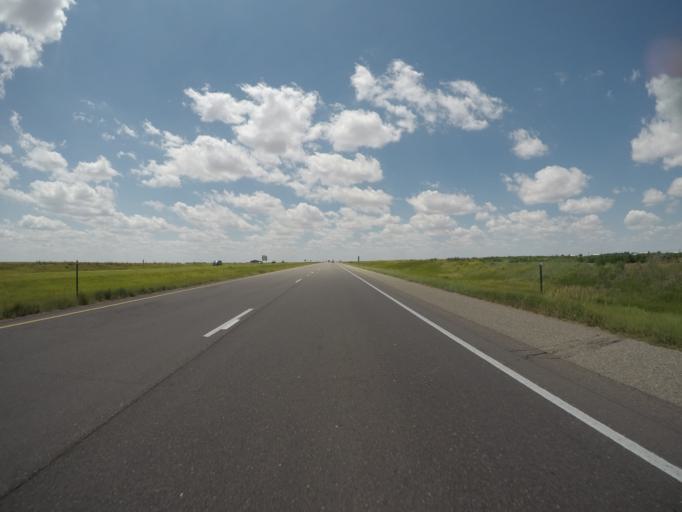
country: US
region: Colorado
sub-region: Kit Carson County
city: Burlington
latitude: 39.2943
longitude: -102.2927
